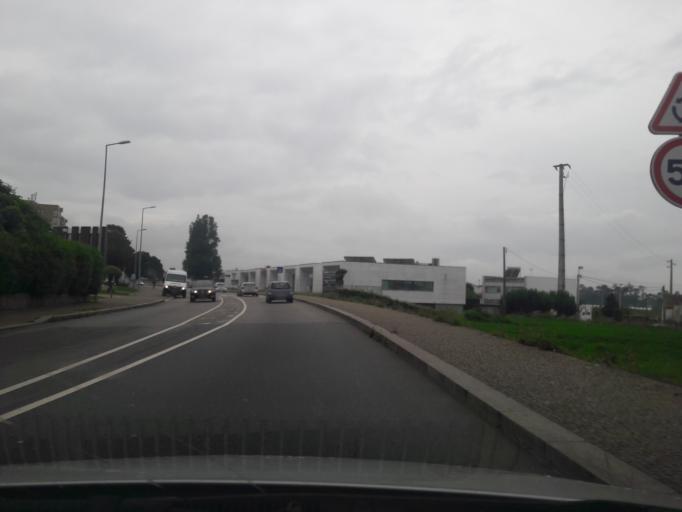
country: PT
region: Porto
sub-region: Vila do Conde
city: Vila do Conde
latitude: 41.3432
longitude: -8.7359
